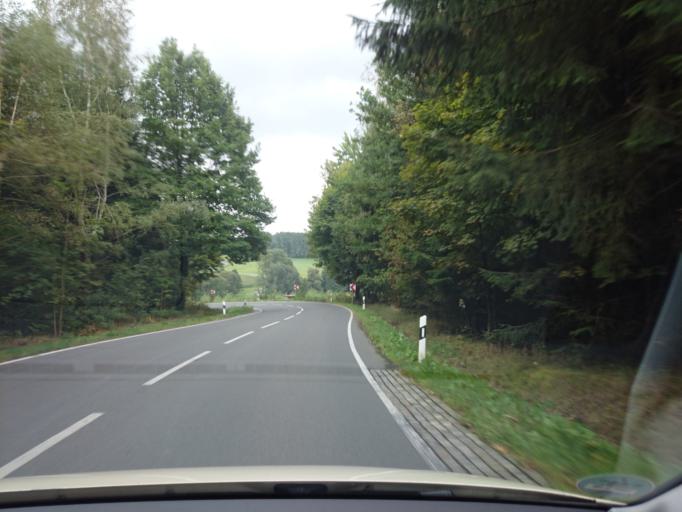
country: DE
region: Saxony
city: Eppendorf
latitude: 50.8005
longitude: 13.2090
